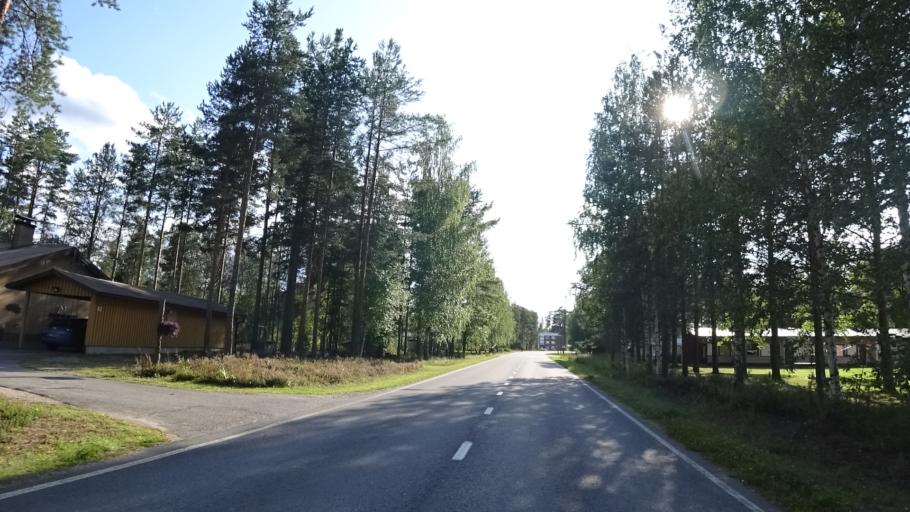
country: FI
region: North Karelia
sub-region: Keski-Karjala
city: Kesaelahti
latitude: 61.8925
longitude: 29.8431
